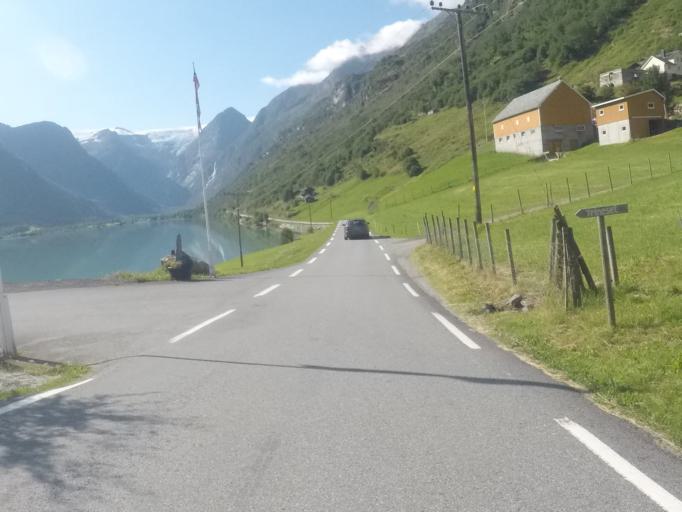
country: NO
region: Sogn og Fjordane
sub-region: Stryn
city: Stryn
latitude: 61.7229
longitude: 6.7944
